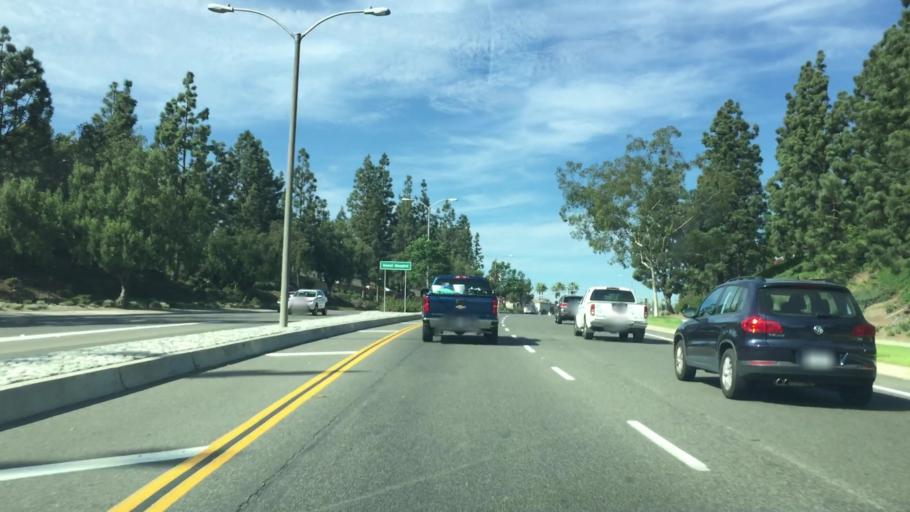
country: US
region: California
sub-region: Orange County
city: Laguna Niguel
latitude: 33.5202
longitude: -117.6851
